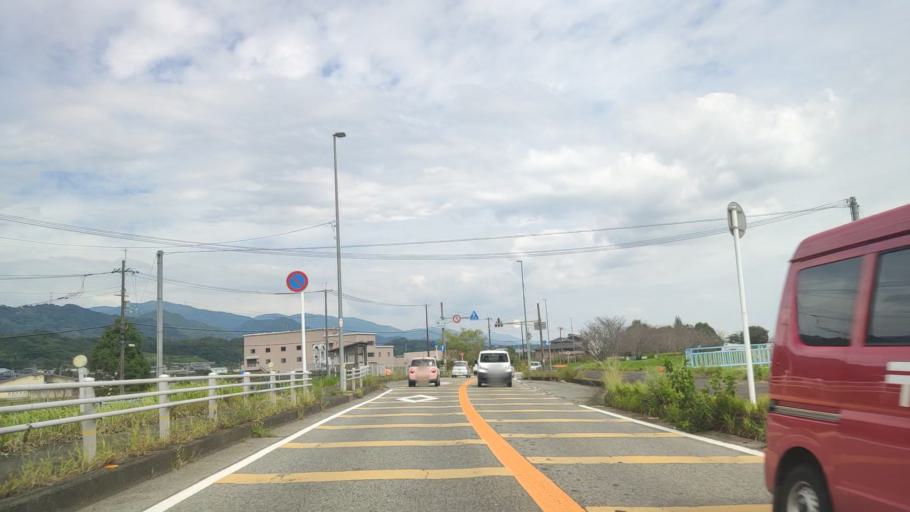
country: JP
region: Wakayama
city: Iwade
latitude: 34.2836
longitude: 135.4606
